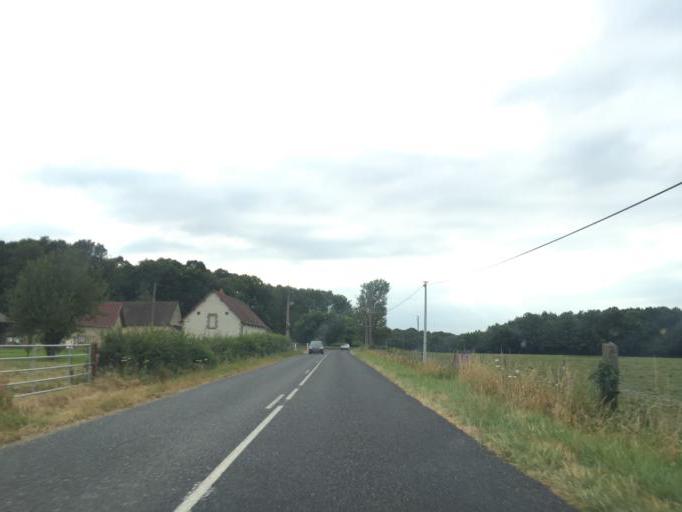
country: FR
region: Auvergne
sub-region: Departement de l'Allier
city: Lusigny
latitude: 46.5314
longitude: 3.4552
